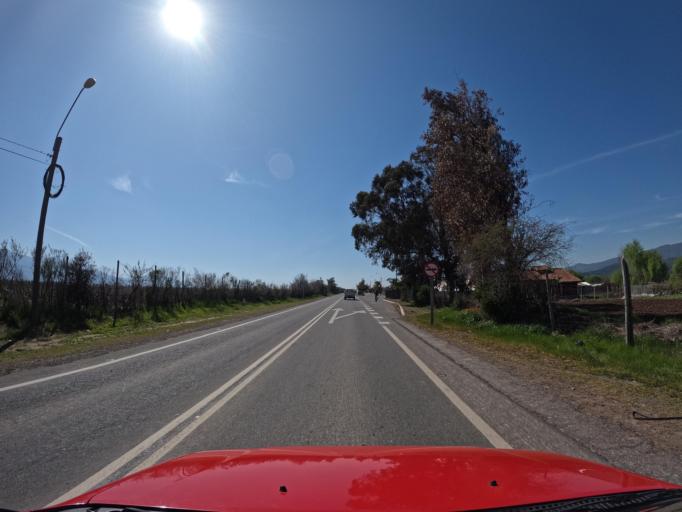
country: CL
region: Maule
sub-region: Provincia de Curico
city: Rauco
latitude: -35.0452
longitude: -71.4626
